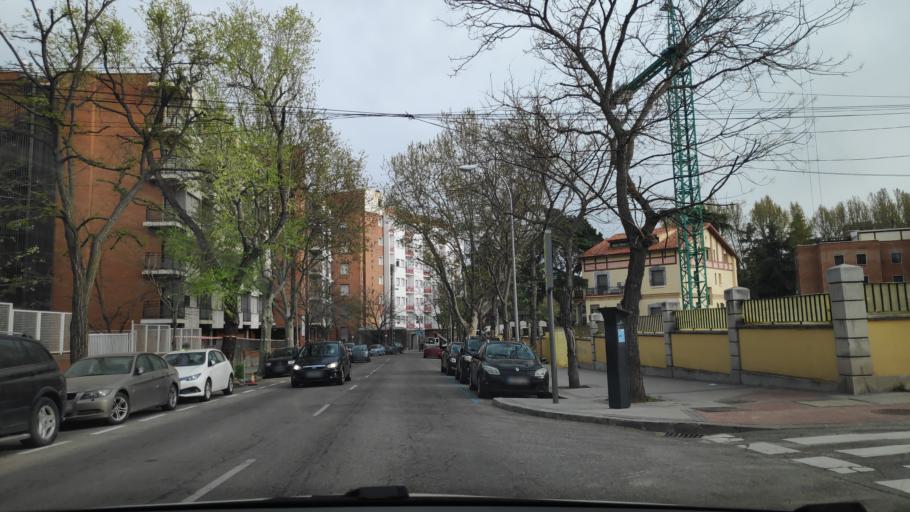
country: ES
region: Madrid
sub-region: Provincia de Madrid
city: Moncloa-Aravaca
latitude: 40.4443
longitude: -3.7198
